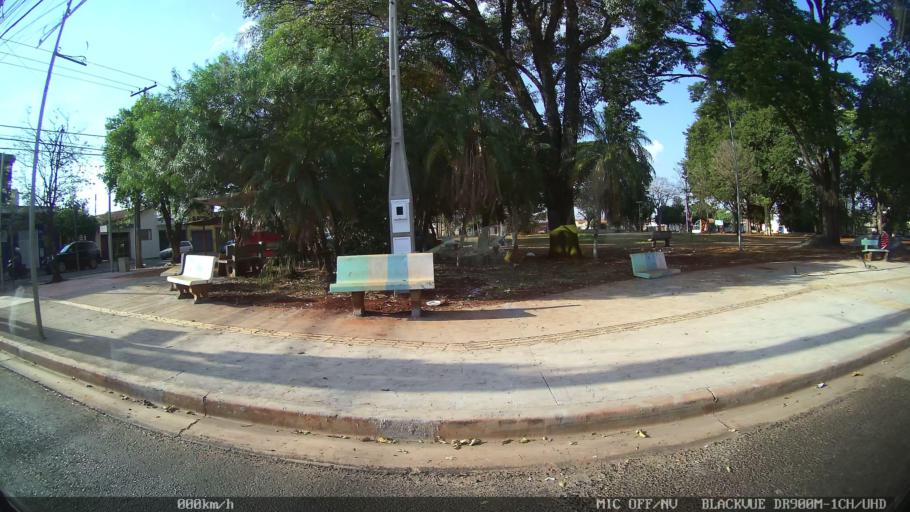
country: BR
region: Sao Paulo
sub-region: Ribeirao Preto
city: Ribeirao Preto
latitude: -21.1581
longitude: -47.8165
